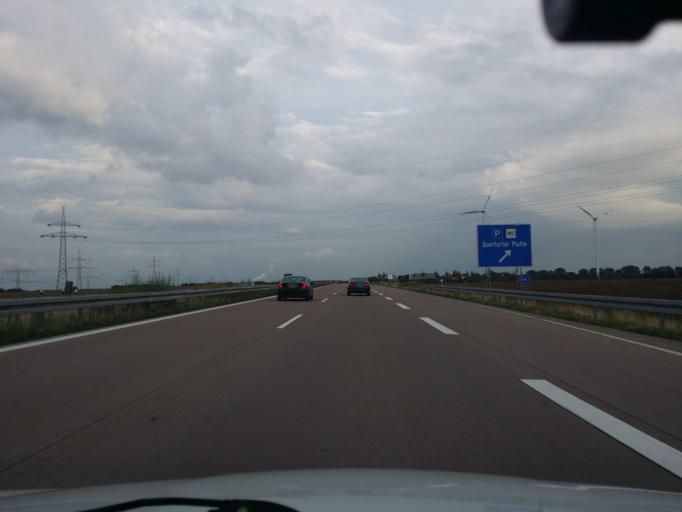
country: DE
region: Saxony-Anhalt
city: Stedten
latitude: 51.4005
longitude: 11.7206
